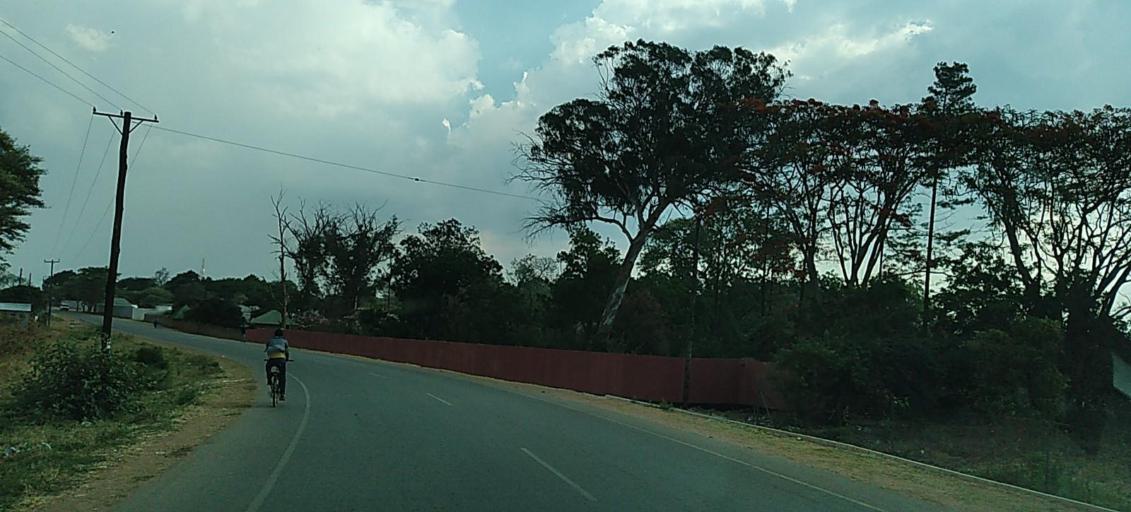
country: ZM
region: Lusaka
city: Lusaka
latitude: -15.5210
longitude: 28.2346
